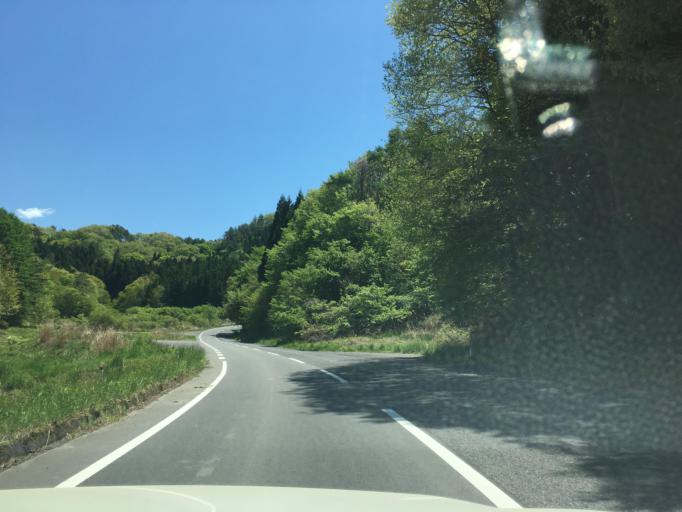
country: JP
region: Fukushima
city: Funehikimachi-funehiki
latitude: 37.3896
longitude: 140.6086
